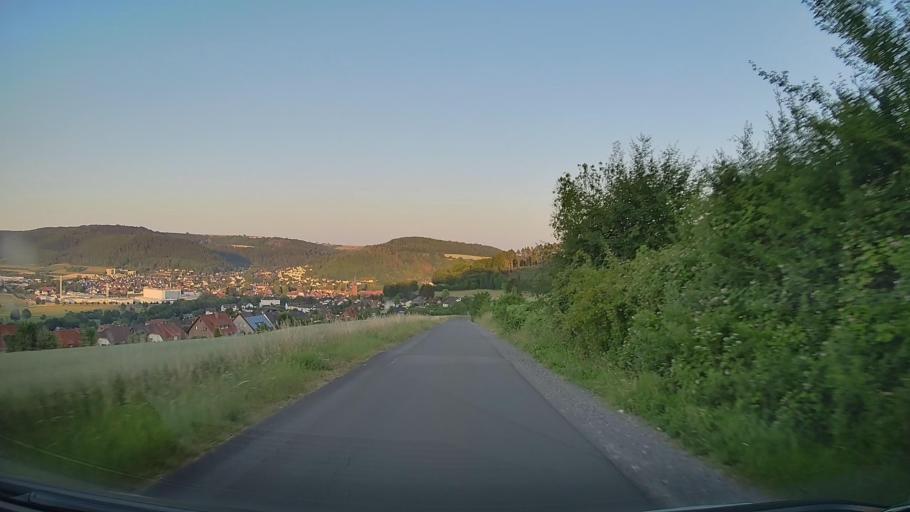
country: DE
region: North Rhine-Westphalia
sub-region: Regierungsbezirk Detmold
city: Lugde
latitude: 51.9641
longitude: 9.2279
